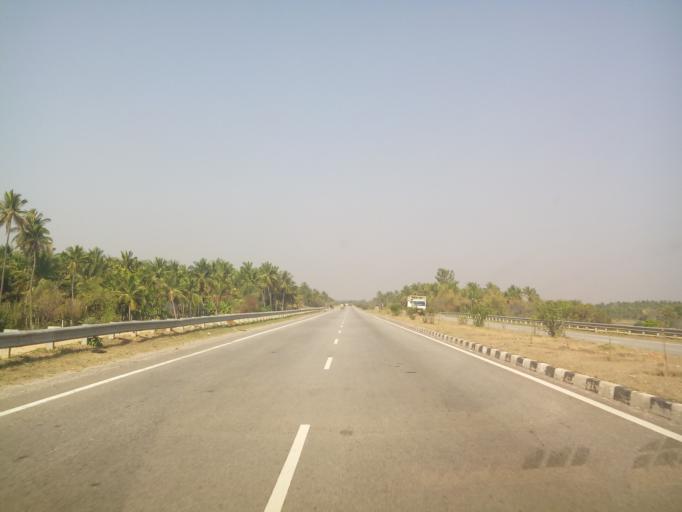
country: IN
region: Karnataka
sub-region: Tumkur
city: Kunigal
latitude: 13.0052
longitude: 76.9903
